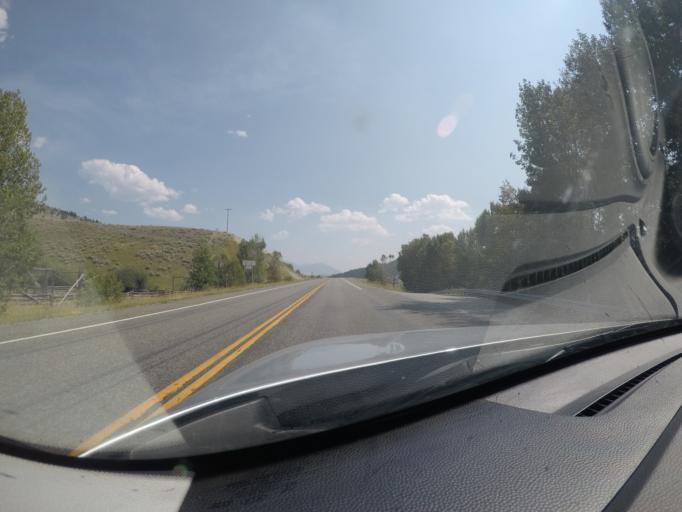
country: US
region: Montana
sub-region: Gallatin County
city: Big Sky
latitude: 44.8914
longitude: -111.5810
